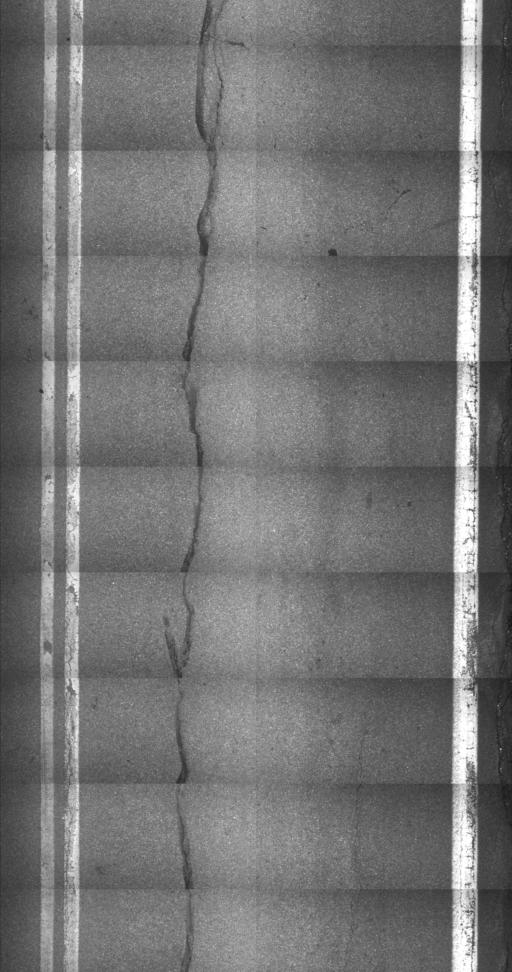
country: US
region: Vermont
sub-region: Rutland County
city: Castleton
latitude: 43.6719
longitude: -73.1917
